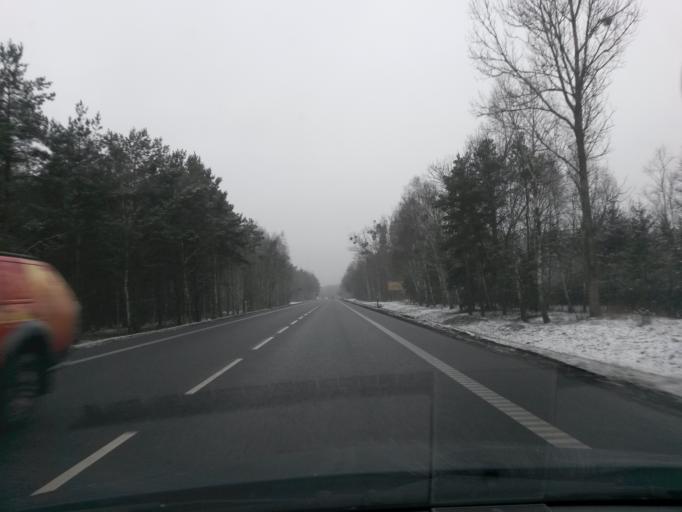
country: PL
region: Kujawsko-Pomorskie
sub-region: Powiat bydgoski
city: Solec Kujawski
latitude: 53.0597
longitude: 18.2248
